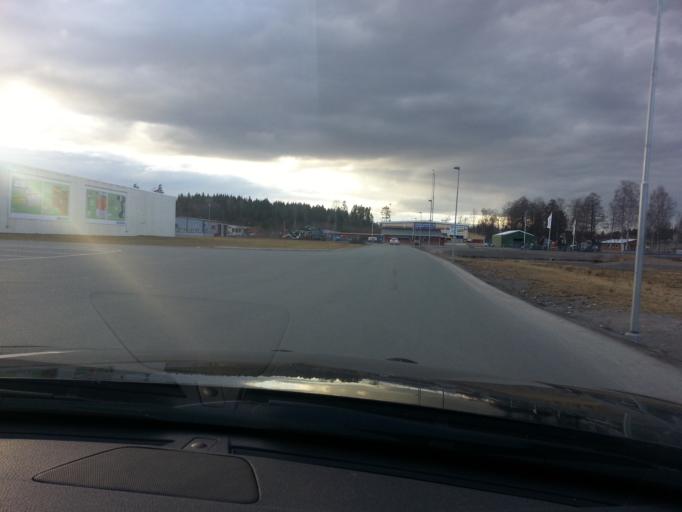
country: SE
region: Joenkoeping
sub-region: Vetlanda Kommun
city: Vetlanda
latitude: 57.4414
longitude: 15.0628
